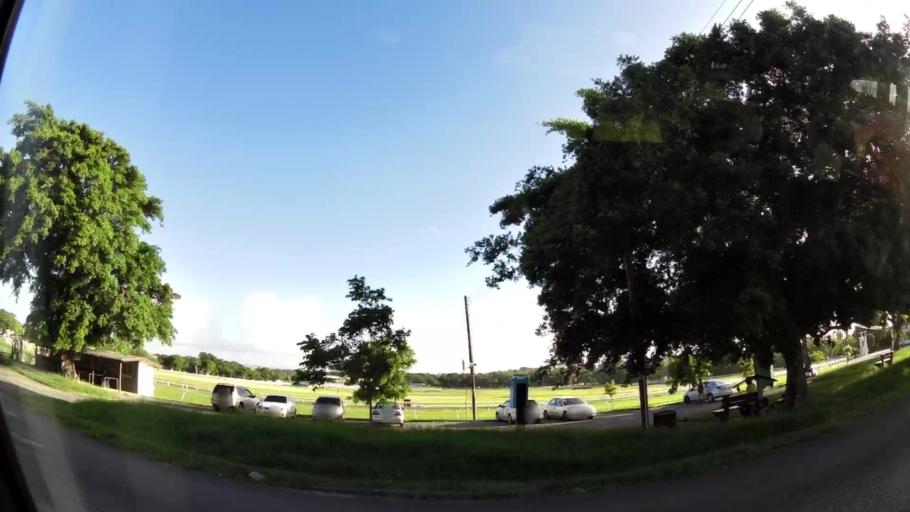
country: BB
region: Saint Michael
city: Bridgetown
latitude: 13.0789
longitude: -59.6060
